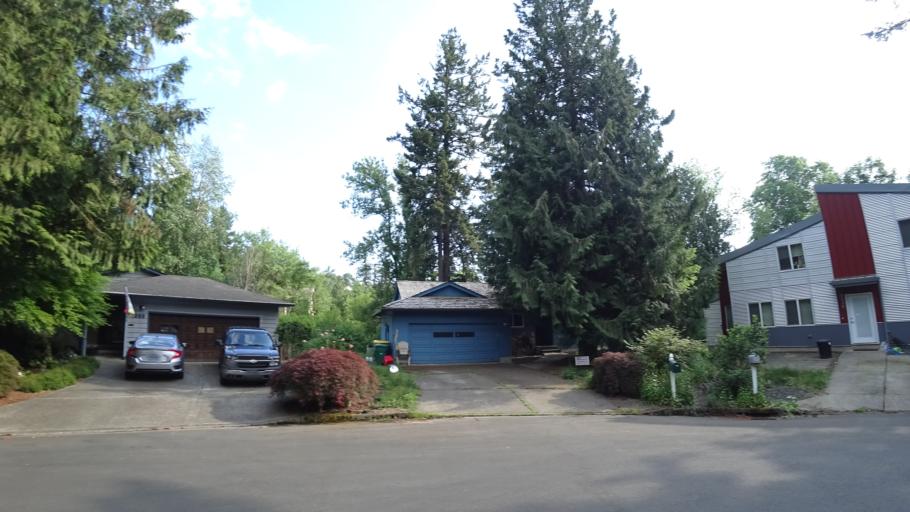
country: US
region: Oregon
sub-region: Washington County
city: Garden Home-Whitford
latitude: 45.4608
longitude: -122.7493
